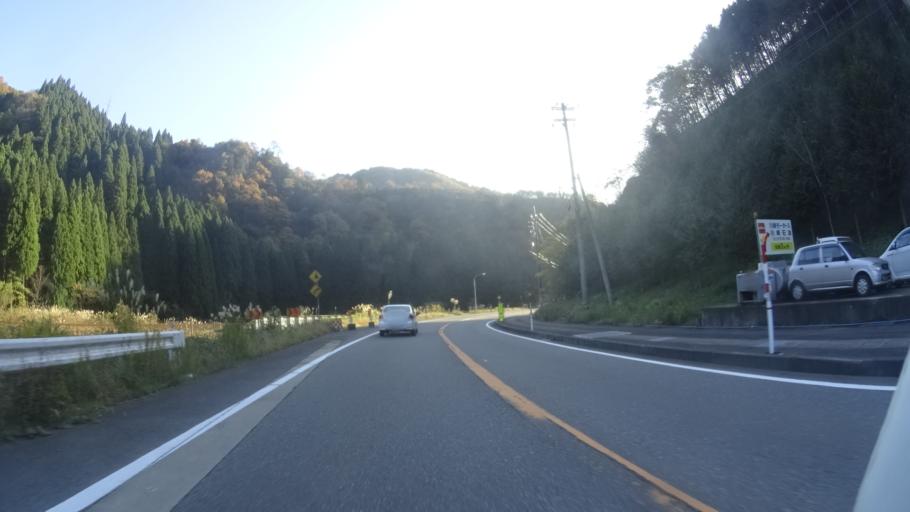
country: JP
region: Fukui
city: Ono
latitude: 36.0036
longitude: 136.3810
